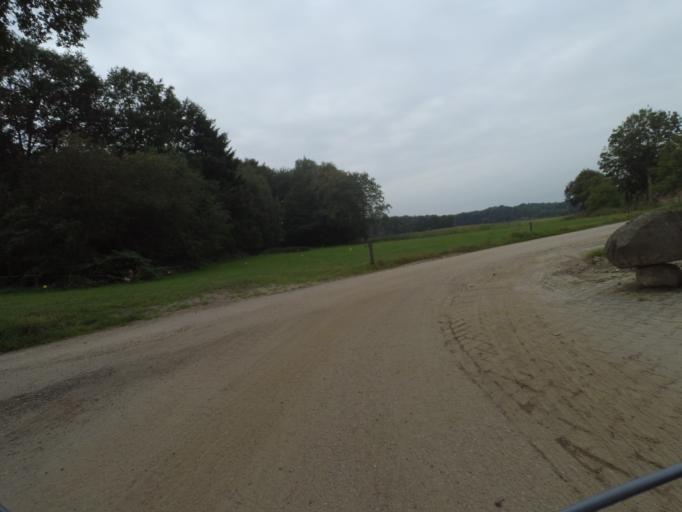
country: NL
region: Overijssel
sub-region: Gemeente Oldenzaal
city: Oldenzaal
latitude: 52.3251
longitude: 6.9763
